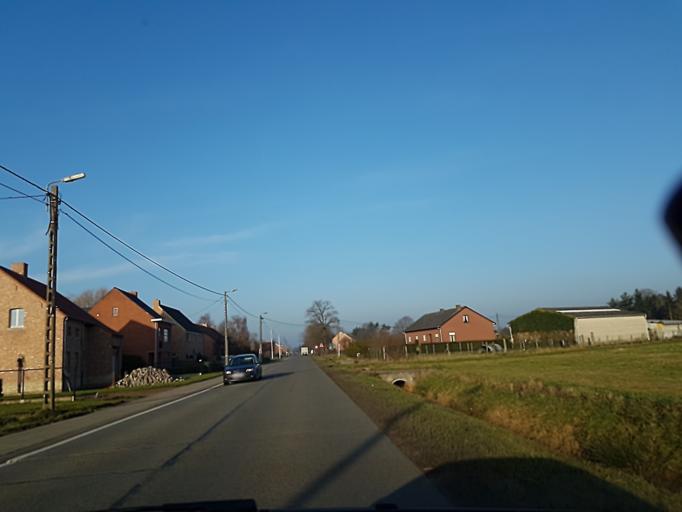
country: BE
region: Flanders
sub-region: Provincie Vlaams-Brabant
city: Tremelo
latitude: 51.0252
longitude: 4.7108
